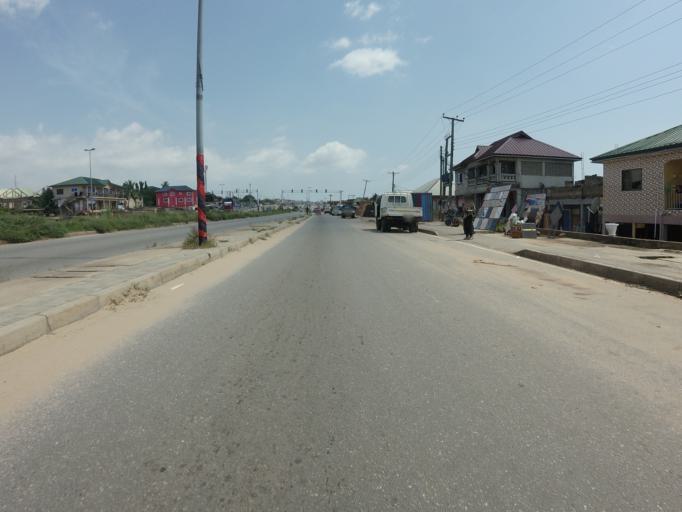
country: GH
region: Greater Accra
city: Gbawe
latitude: 5.6263
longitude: -0.3082
